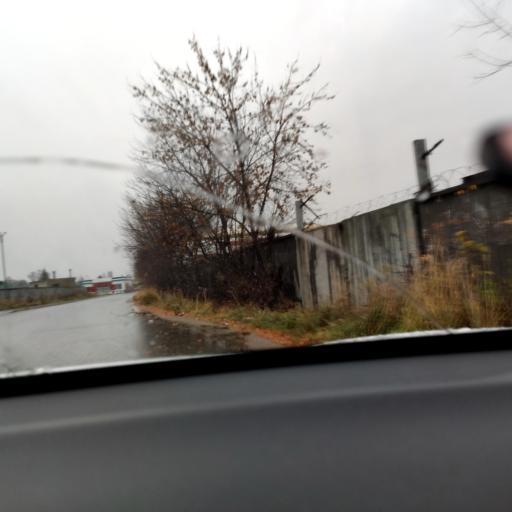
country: RU
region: Tatarstan
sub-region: Gorod Kazan'
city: Kazan
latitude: 55.8665
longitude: 49.1093
